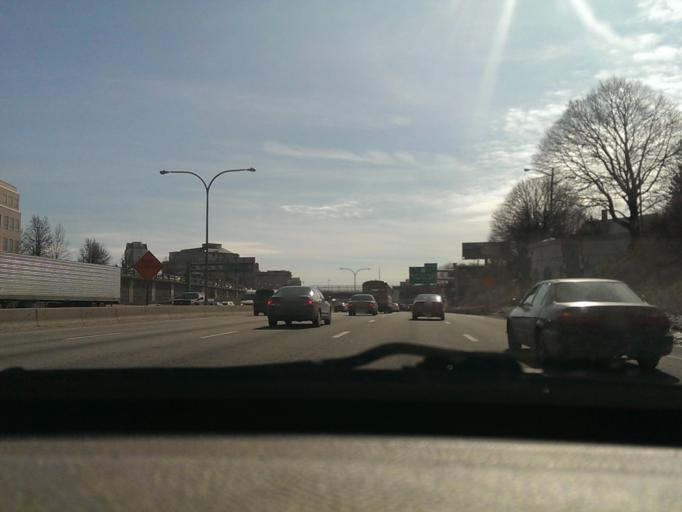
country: US
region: Rhode Island
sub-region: Providence County
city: Providence
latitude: 41.8339
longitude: -71.4166
